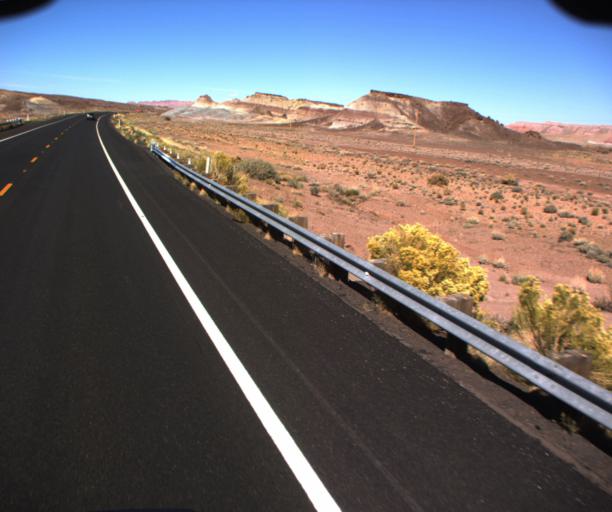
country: US
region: Arizona
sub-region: Coconino County
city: Tuba City
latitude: 36.0981
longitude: -111.3957
